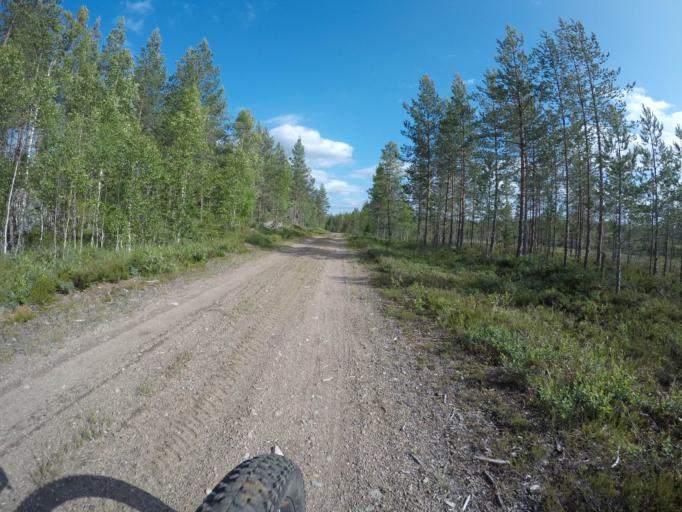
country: SE
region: OErebro
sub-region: Hallefors Kommun
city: Haellefors
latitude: 60.0732
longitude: 14.5135
